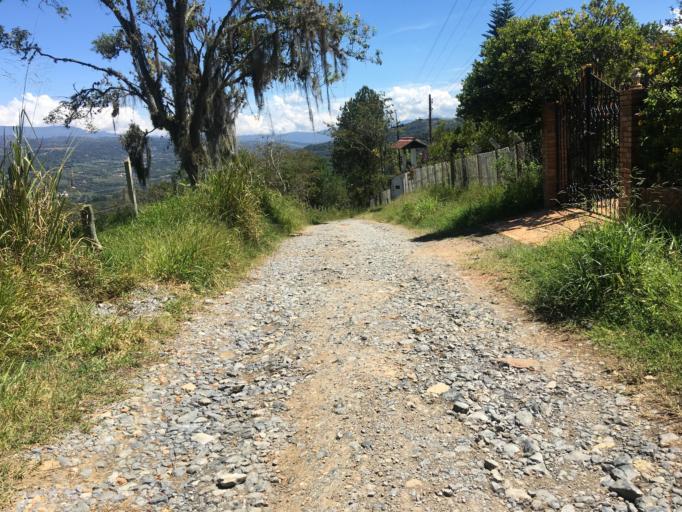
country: CO
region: Santander
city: Barbosa
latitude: 5.9127
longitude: -73.5983
